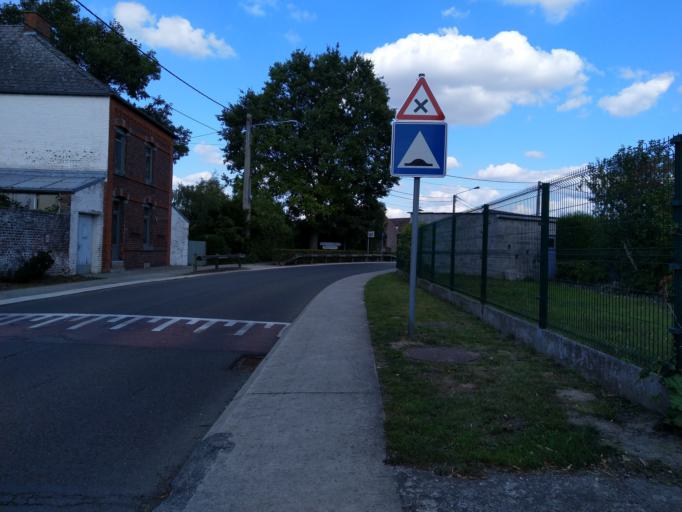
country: BE
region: Wallonia
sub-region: Province du Hainaut
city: Lens
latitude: 50.5290
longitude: 3.8604
